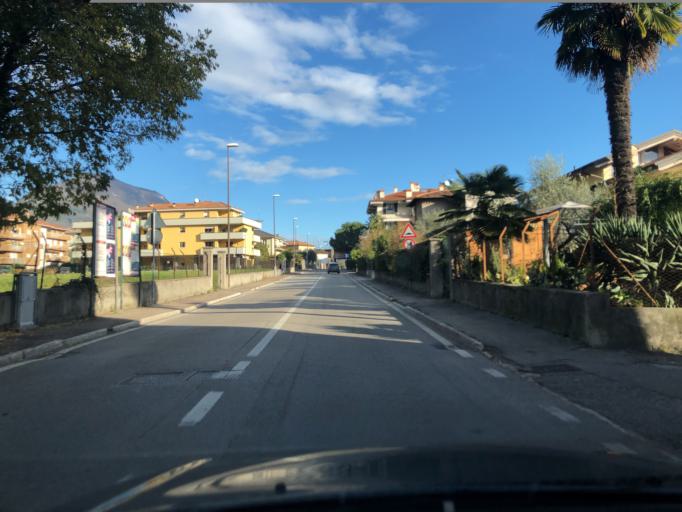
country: IT
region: Trentino-Alto Adige
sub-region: Provincia di Trento
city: Riva del Garda
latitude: 45.8909
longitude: 10.8506
